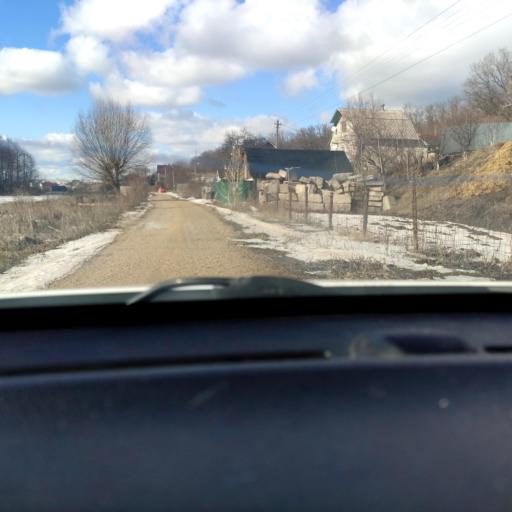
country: RU
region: Voronezj
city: Novaya Usman'
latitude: 51.6873
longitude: 39.3877
